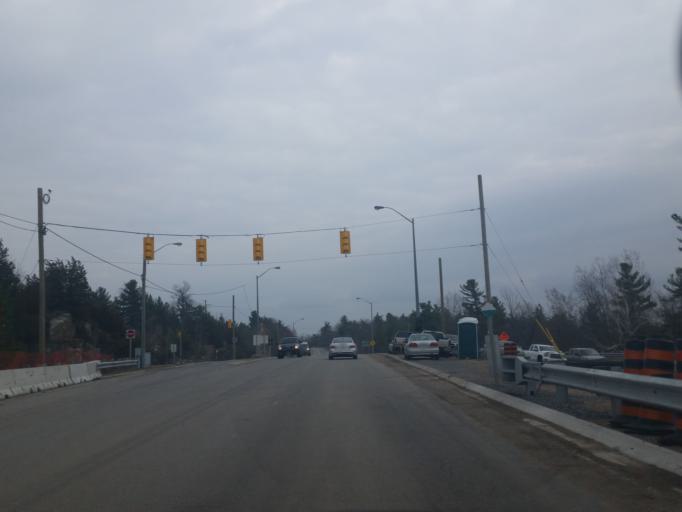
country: US
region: New York
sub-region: Jefferson County
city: Alexandria Bay
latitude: 44.3689
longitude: -75.9788
